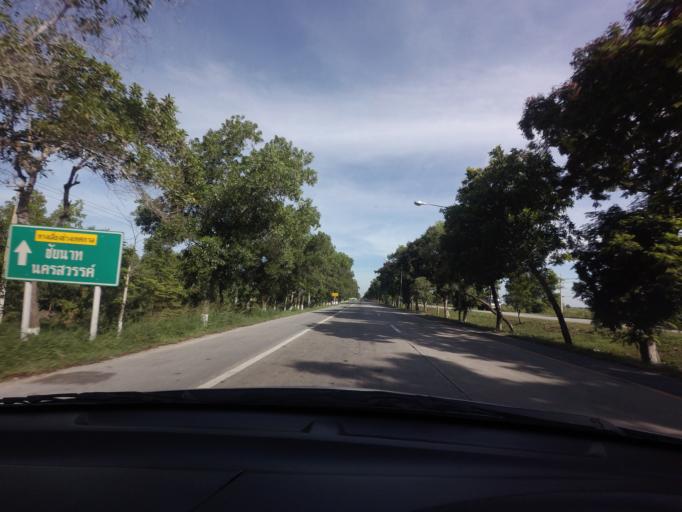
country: TH
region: Suphan Buri
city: Bang Pla Ma
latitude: 14.3315
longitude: 100.2085
